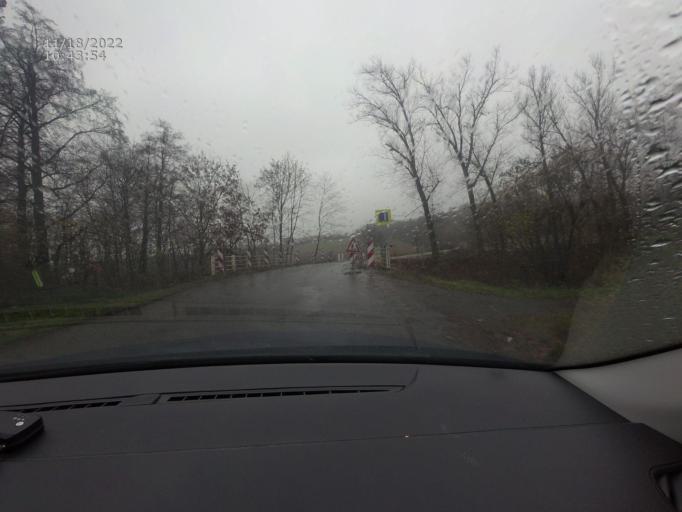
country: CZ
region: Central Bohemia
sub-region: Okres Beroun
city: Horovice
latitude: 49.8443
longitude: 13.9099
